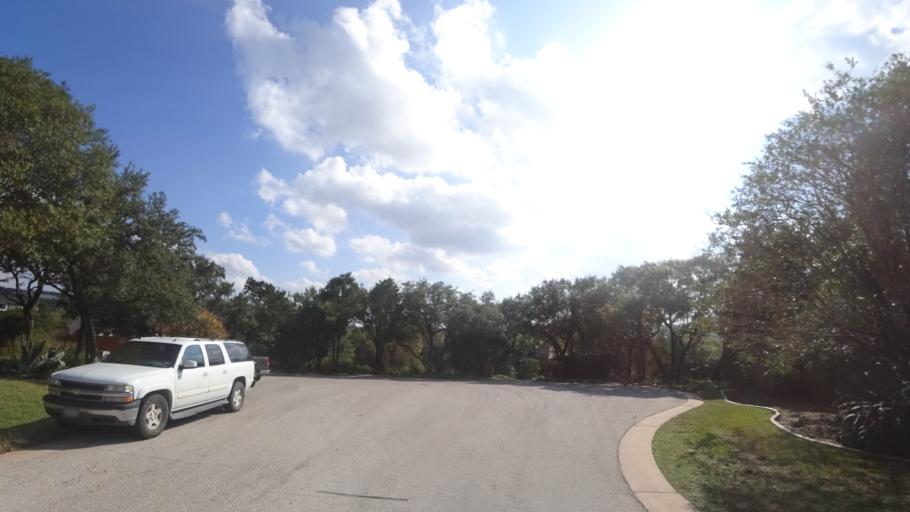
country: US
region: Texas
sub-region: Travis County
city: Lost Creek
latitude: 30.3069
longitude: -97.8537
